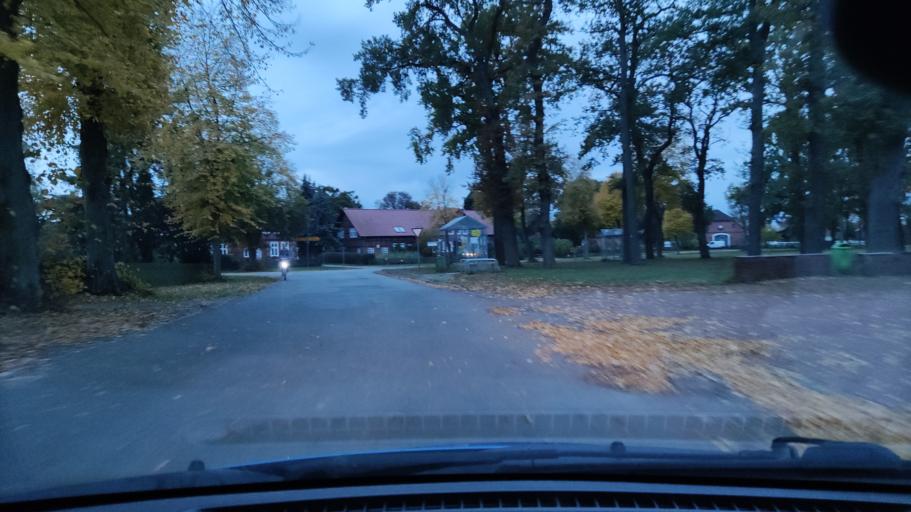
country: DE
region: Lower Saxony
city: Prezelle
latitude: 52.9623
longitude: 11.4020
